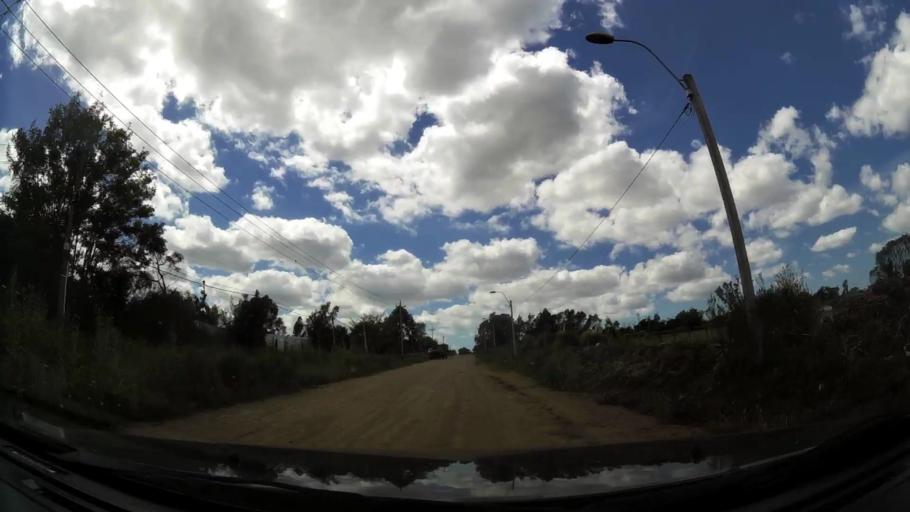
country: UY
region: Canelones
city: Colonia Nicolich
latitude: -34.8154
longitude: -56.0454
